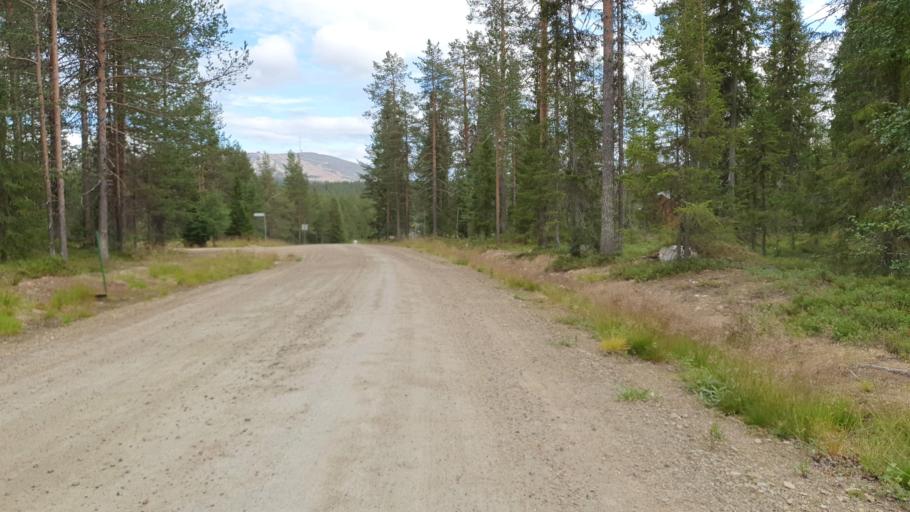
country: FI
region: Lapland
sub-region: Tunturi-Lappi
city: Kolari
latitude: 67.5997
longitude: 24.1357
